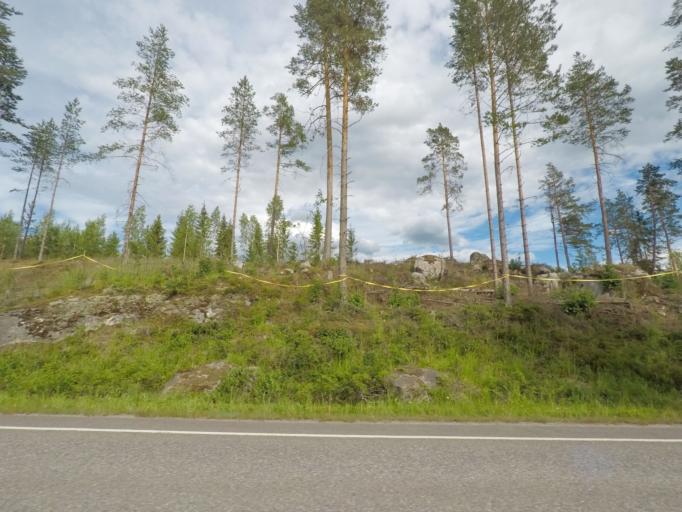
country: FI
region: Paijanne Tavastia
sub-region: Lahti
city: Hollola
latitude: 60.8312
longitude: 25.4905
